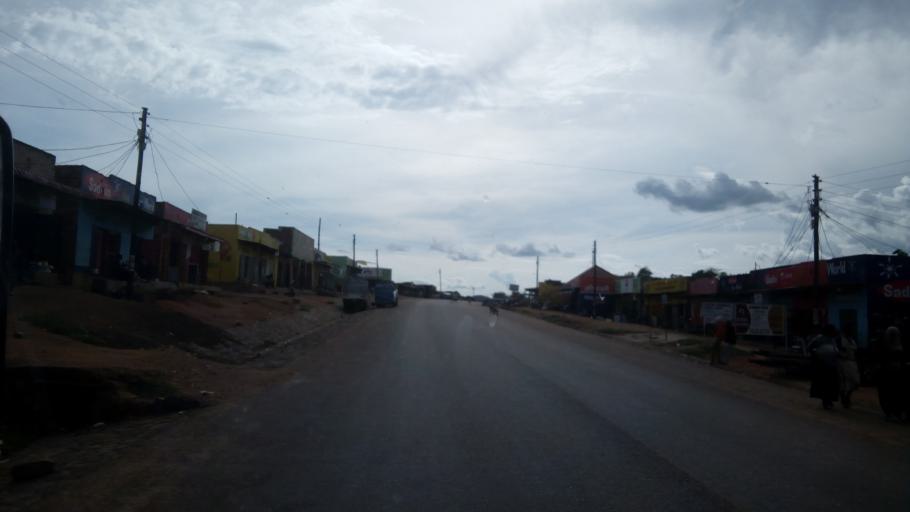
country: UG
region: Western Region
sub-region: Kyegegwa District
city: Kyegegwa
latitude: 0.4872
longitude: 31.1825
